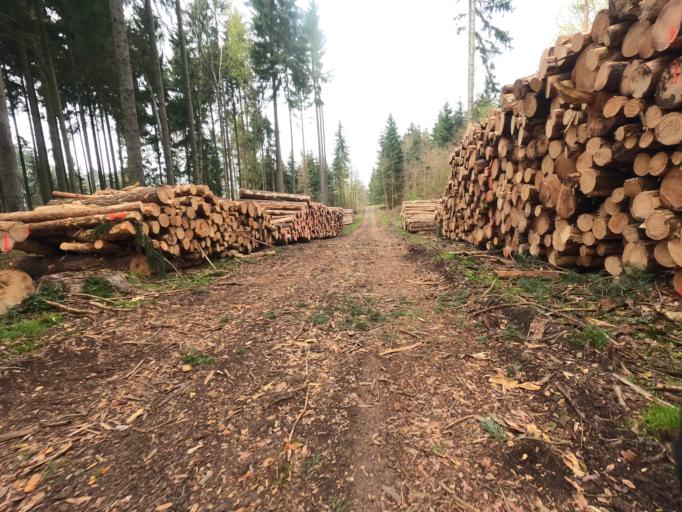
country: PL
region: West Pomeranian Voivodeship
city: Trzcinsko Zdroj
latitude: 52.9120
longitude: 14.5671
